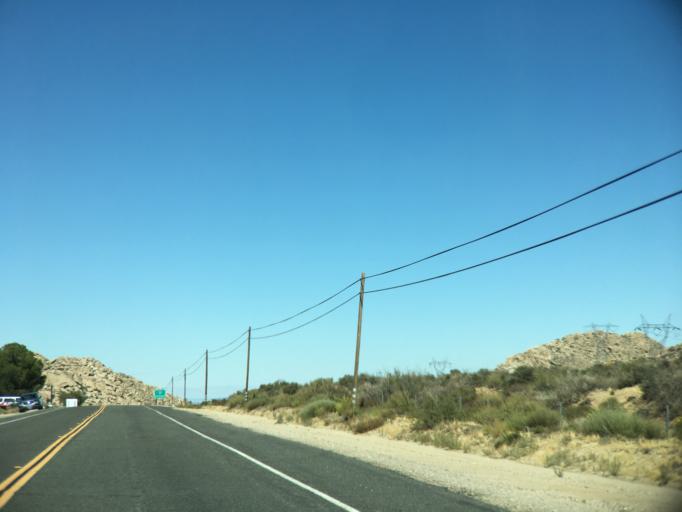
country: MX
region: Baja California
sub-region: Tecate
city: Cereso del Hongo
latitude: 32.6443
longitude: -116.1071
